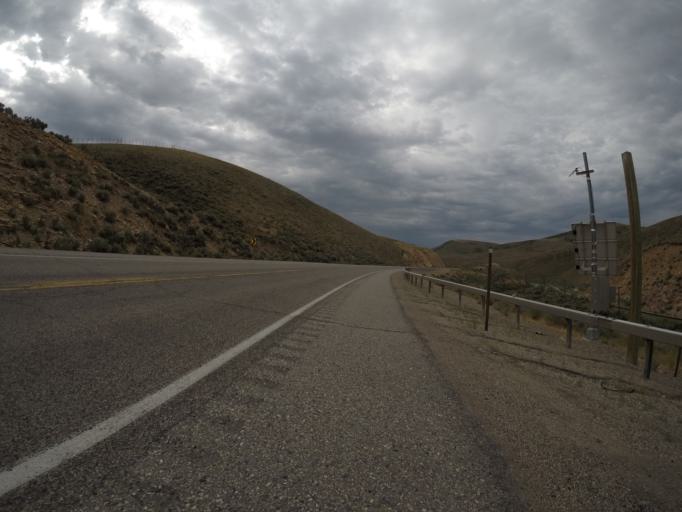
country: US
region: Wyoming
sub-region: Lincoln County
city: Kemmerer
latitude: 41.8243
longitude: -110.8088
